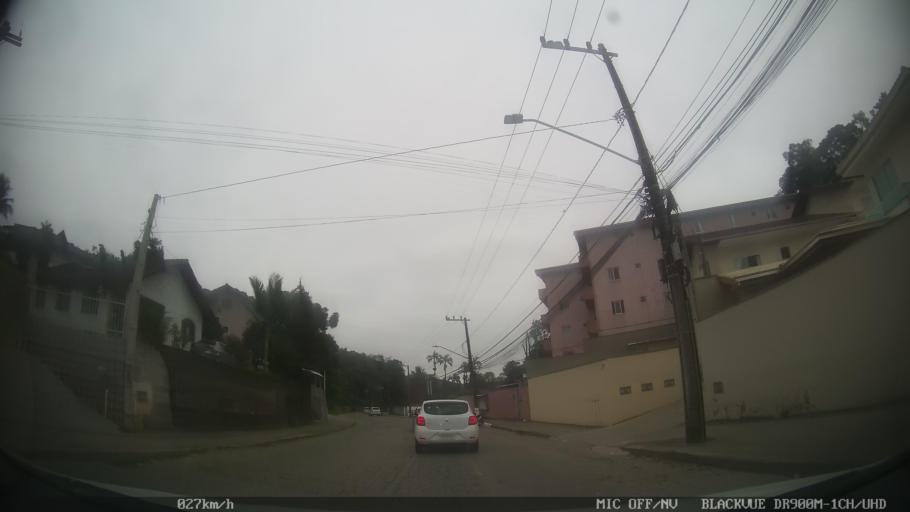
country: BR
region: Santa Catarina
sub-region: Joinville
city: Joinville
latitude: -26.3290
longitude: -48.8572
